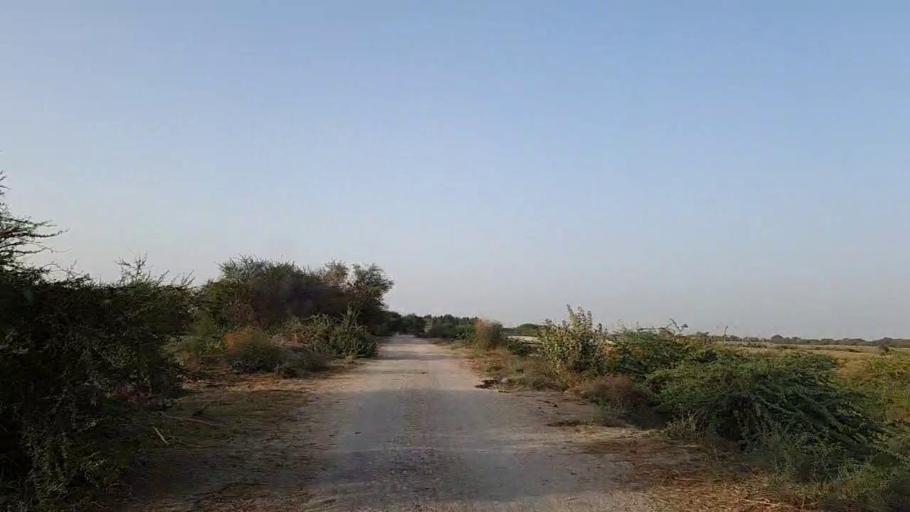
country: PK
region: Sindh
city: Jati
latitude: 24.4137
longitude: 68.1864
